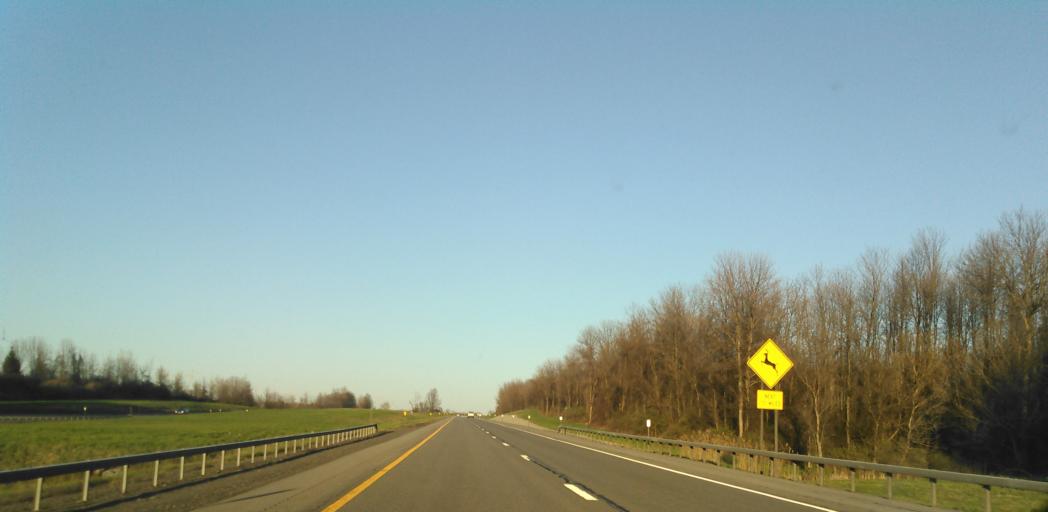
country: US
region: New York
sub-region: Monroe County
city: Pittsford
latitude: 43.0473
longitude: -77.5967
